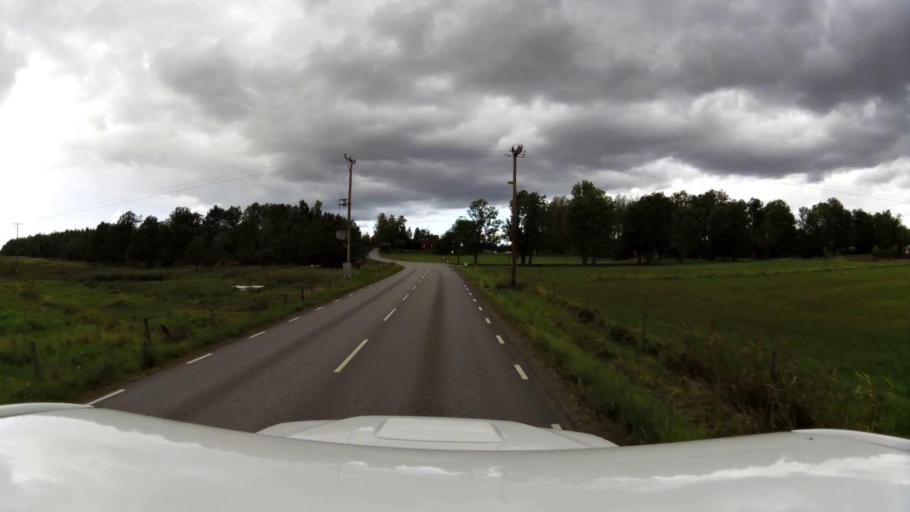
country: SE
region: OEstergoetland
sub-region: Linkopings Kommun
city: Linghem
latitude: 58.4069
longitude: 15.7647
